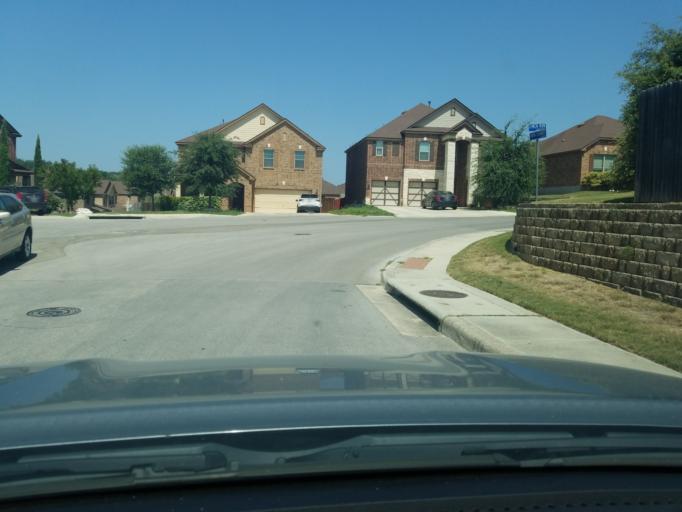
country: US
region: Texas
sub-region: Bexar County
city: Hollywood Park
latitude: 29.6383
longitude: -98.4733
